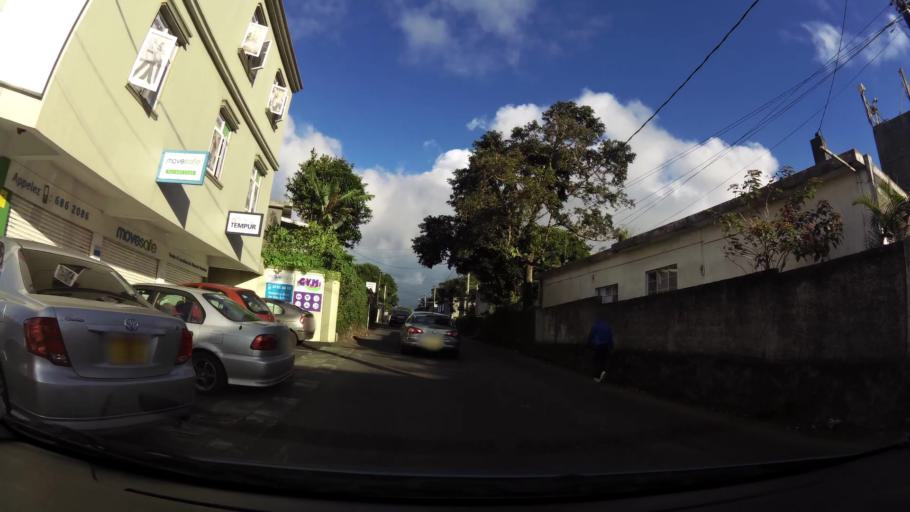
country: MU
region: Plaines Wilhems
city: Curepipe
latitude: -20.3132
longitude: 57.5191
